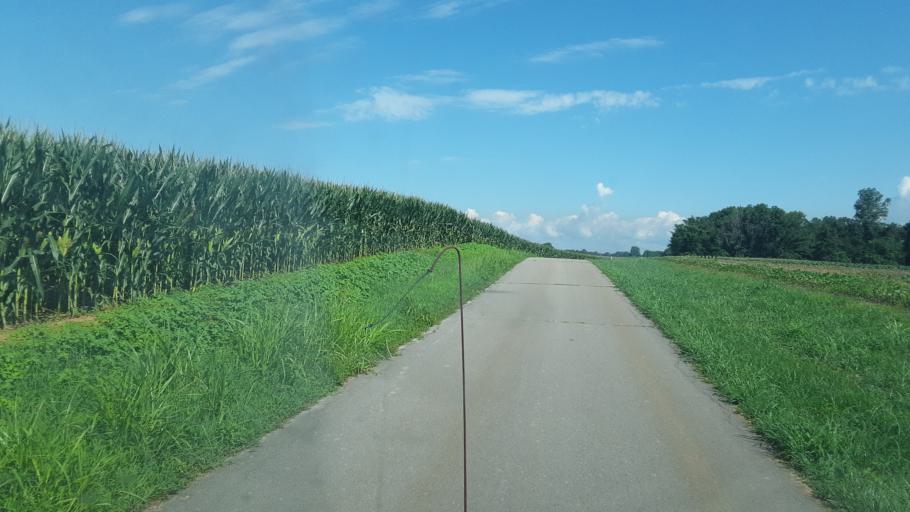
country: US
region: Kentucky
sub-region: Todd County
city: Elkton
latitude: 36.7729
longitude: -87.2308
